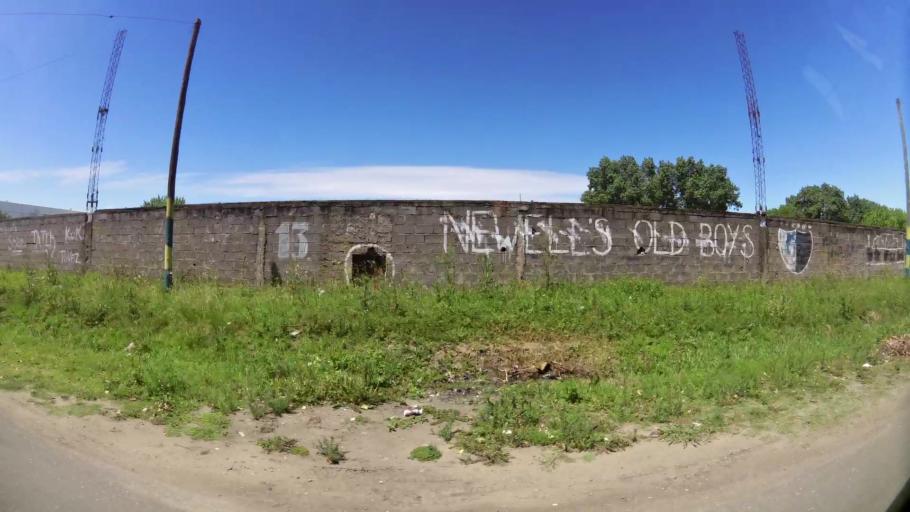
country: AR
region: Santa Fe
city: Perez
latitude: -32.9523
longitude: -60.7139
